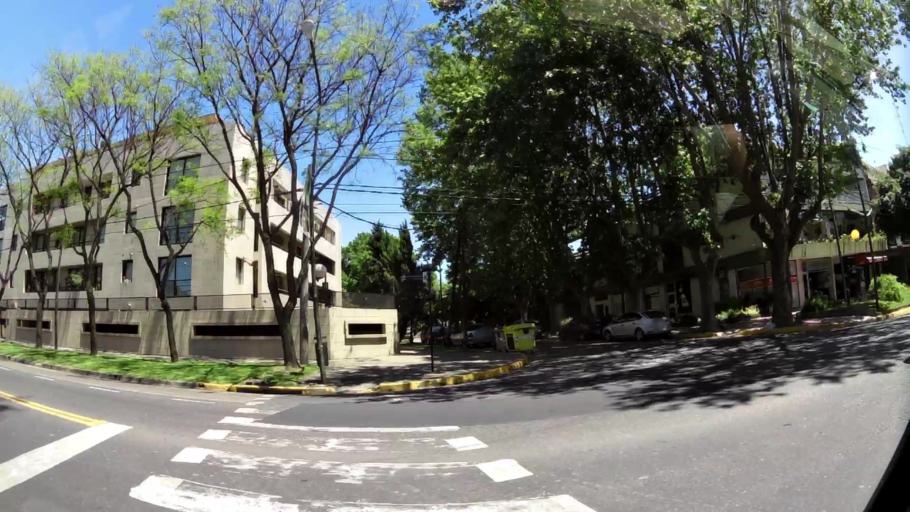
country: AR
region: Buenos Aires
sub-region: Partido de Vicente Lopez
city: Olivos
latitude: -34.4910
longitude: -58.4847
